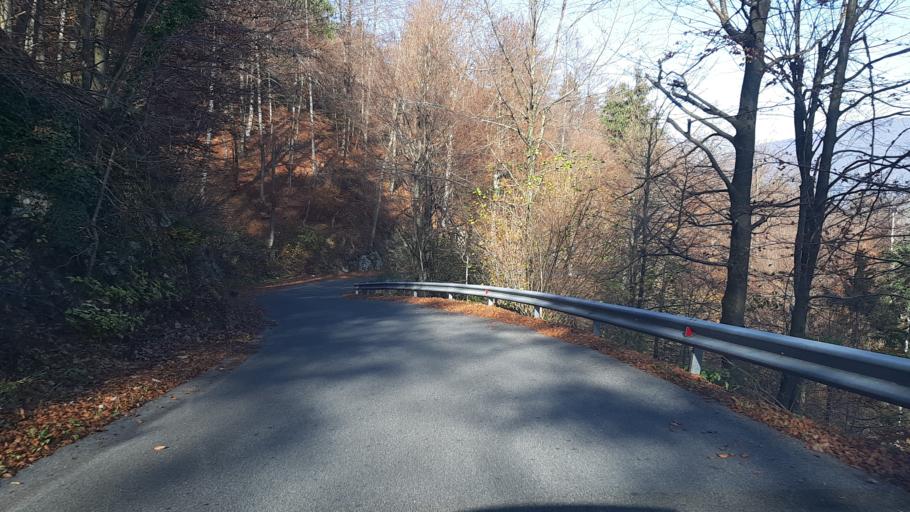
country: SI
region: Borovnica
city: Borovnica
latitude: 45.8966
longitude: 14.3618
